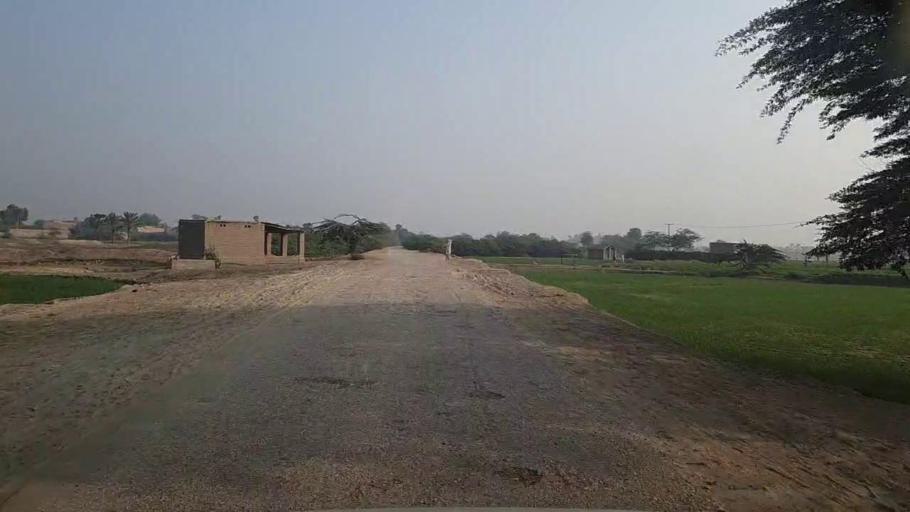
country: PK
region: Sindh
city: Kandiari
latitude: 27.0442
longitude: 68.4740
